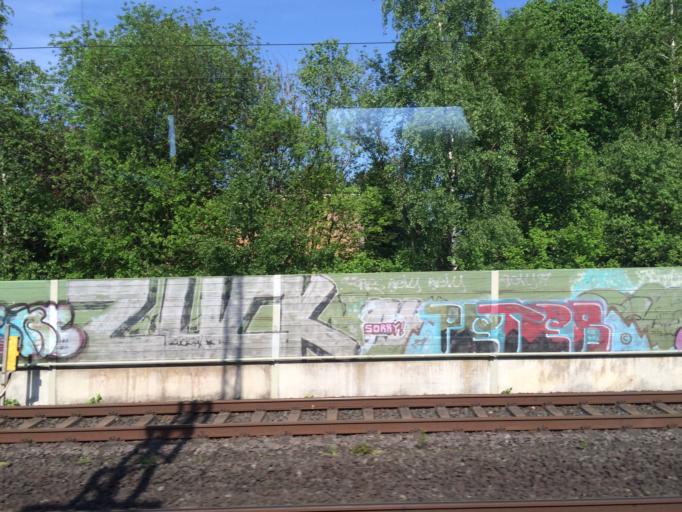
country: DE
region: North Rhine-Westphalia
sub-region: Regierungsbezirk Dusseldorf
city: Langenfeld
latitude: 51.0970
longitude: 6.9418
